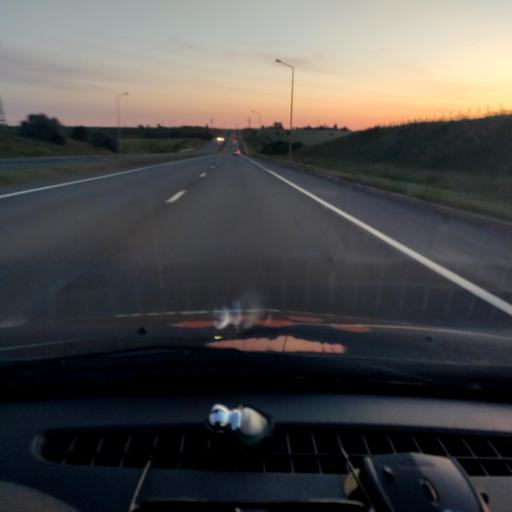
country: RU
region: Belgorod
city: Staryy Oskol
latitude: 51.3249
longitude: 37.7284
